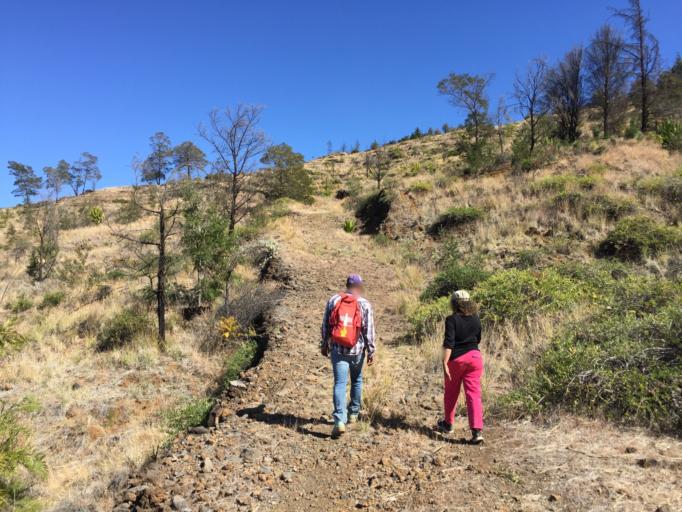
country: CV
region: Mosteiros
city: Porto dos Mosteiros
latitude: 15.0070
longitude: -24.3594
